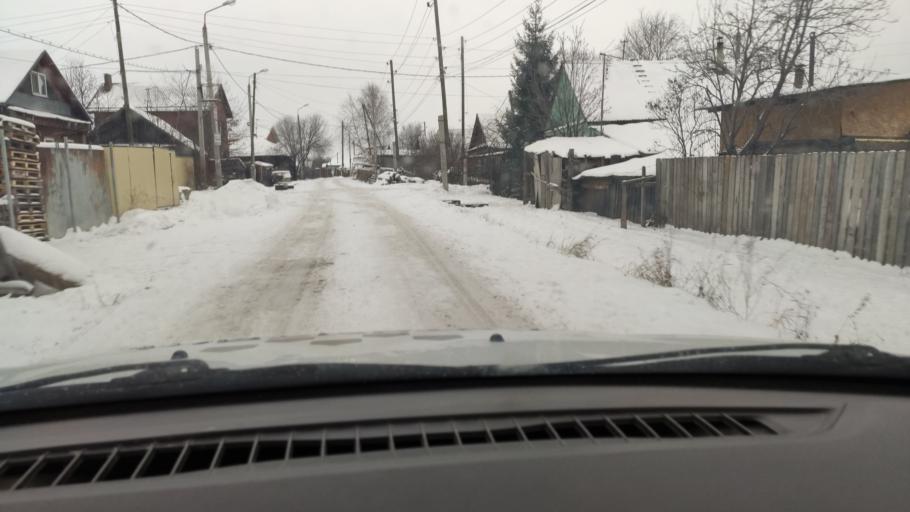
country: RU
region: Perm
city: Kondratovo
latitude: 57.9599
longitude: 56.1242
